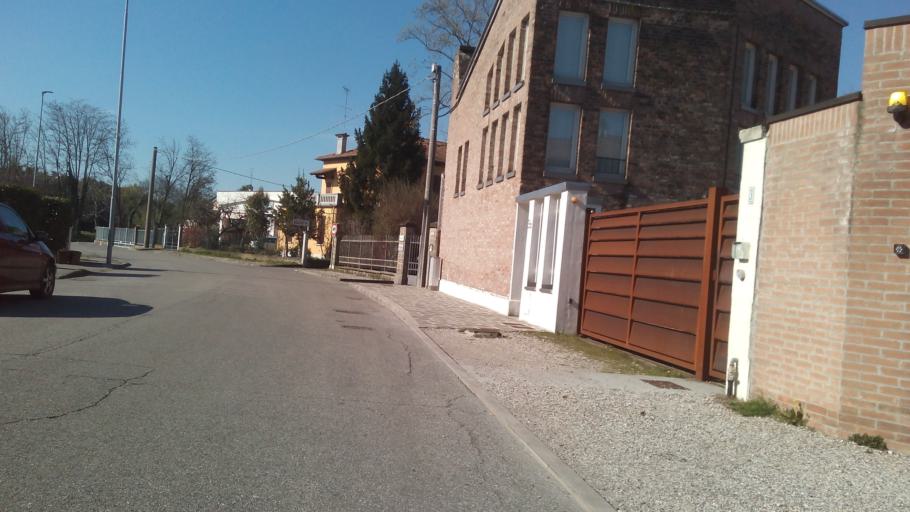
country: IT
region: Lombardy
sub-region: Provincia di Mantova
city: Mantova
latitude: 45.1551
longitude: 10.7690
